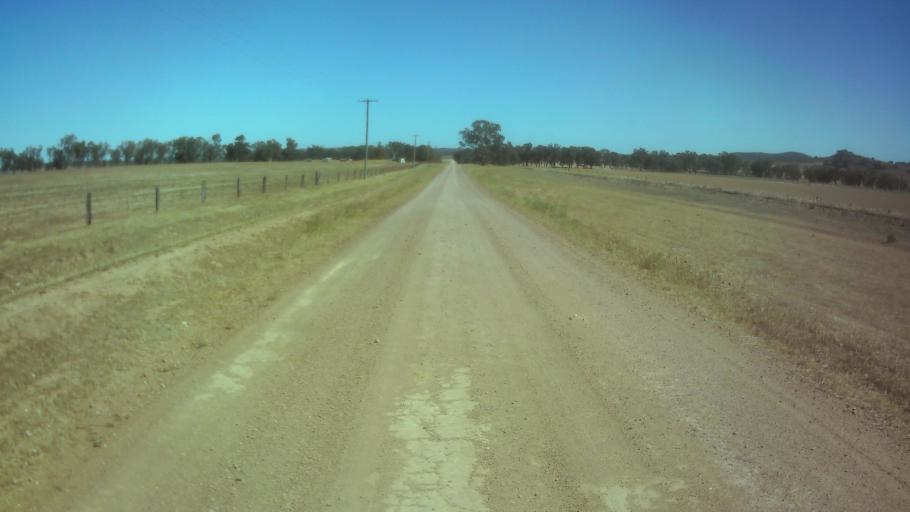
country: AU
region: New South Wales
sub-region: Weddin
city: Grenfell
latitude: -33.9489
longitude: 148.2971
